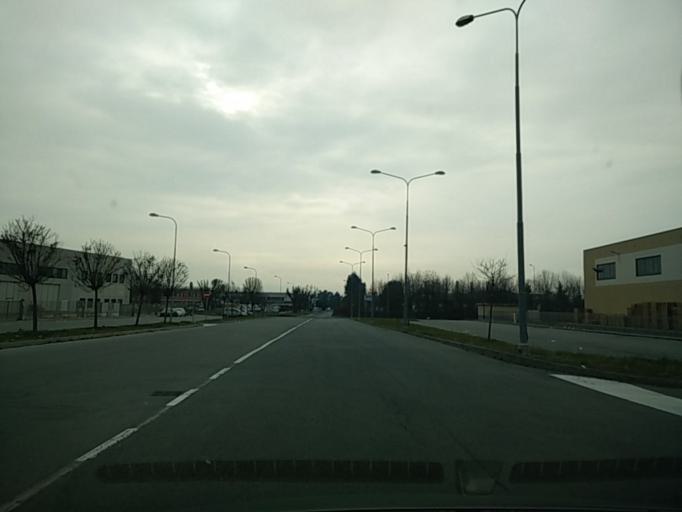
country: IT
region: Piedmont
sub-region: Provincia di Torino
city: Leini
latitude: 45.1519
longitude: 7.7290
